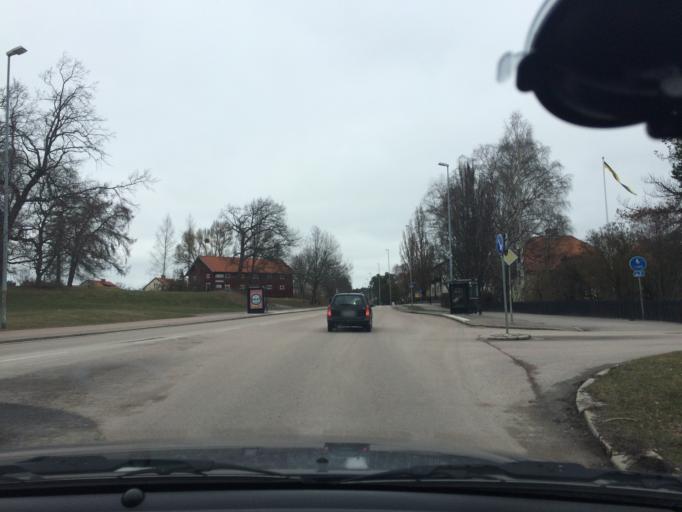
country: SE
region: Vaestmanland
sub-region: Vasteras
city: Vasteras
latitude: 59.6195
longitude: 16.5448
